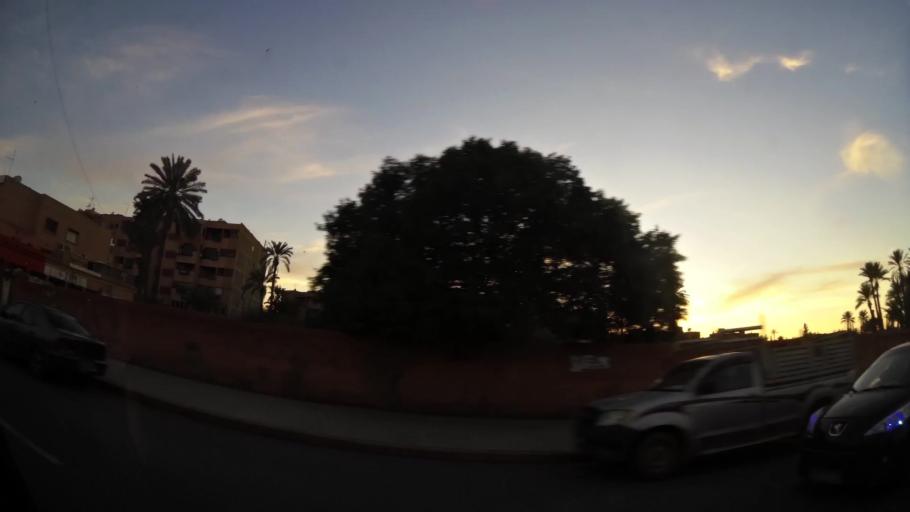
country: MA
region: Marrakech-Tensift-Al Haouz
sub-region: Marrakech
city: Marrakesh
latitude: 31.6423
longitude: -8.0003
